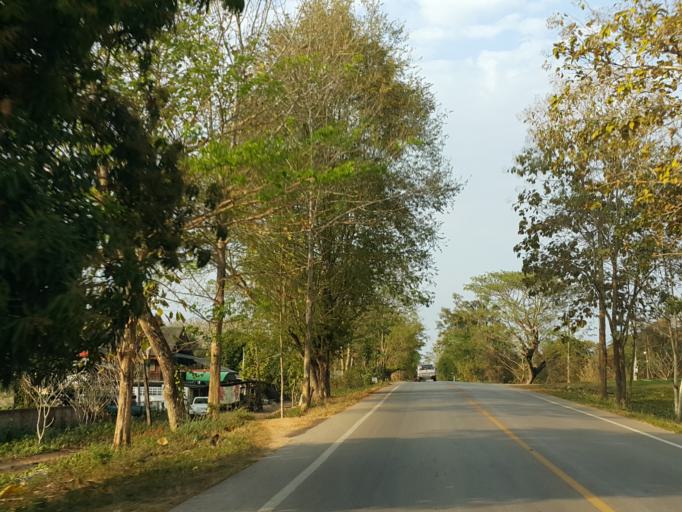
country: TH
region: Lampang
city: Lampang
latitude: 18.5048
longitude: 99.4731
